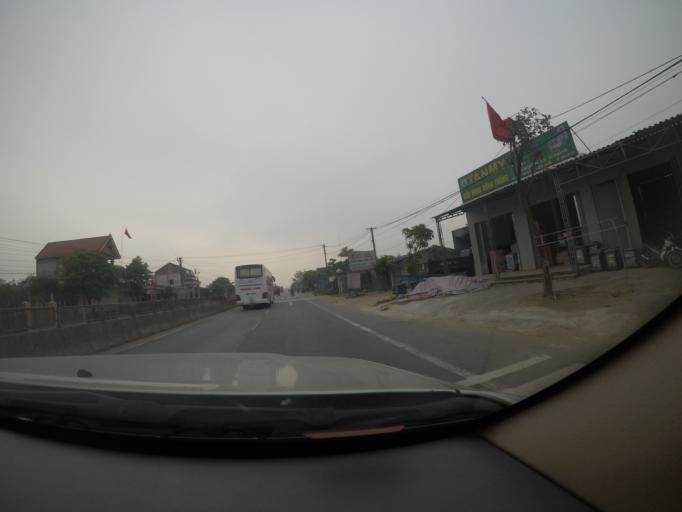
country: VN
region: Ha Tinh
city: Cam Xuyen
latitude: 18.2144
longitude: 106.0997
